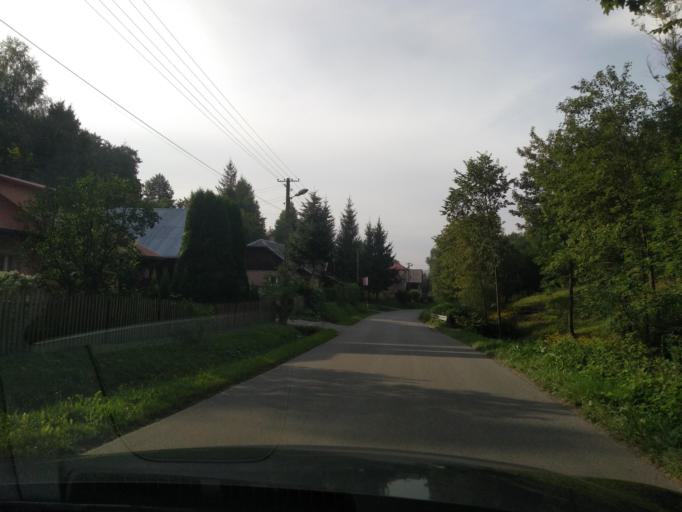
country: PL
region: Subcarpathian Voivodeship
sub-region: Powiat brzozowski
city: Dydnia
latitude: 49.6654
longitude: 22.1931
